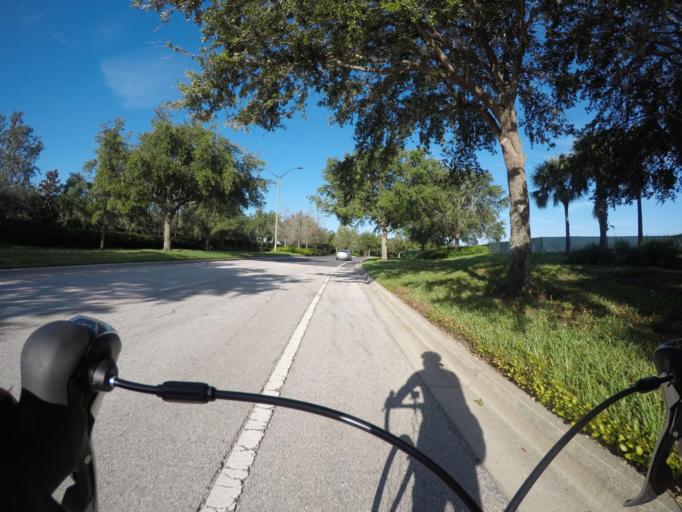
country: US
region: Florida
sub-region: Orange County
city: Meadow Woods
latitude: 28.3971
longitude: -81.2603
